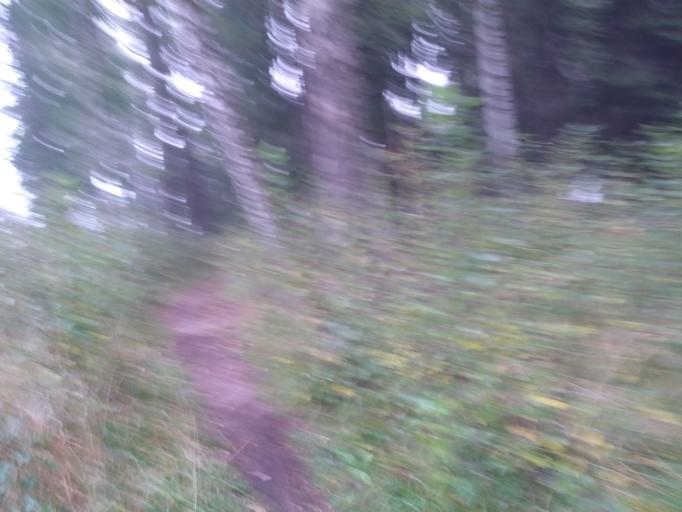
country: SE
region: Uppsala
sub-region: Uppsala Kommun
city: Uppsala
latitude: 59.8383
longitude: 17.6409
